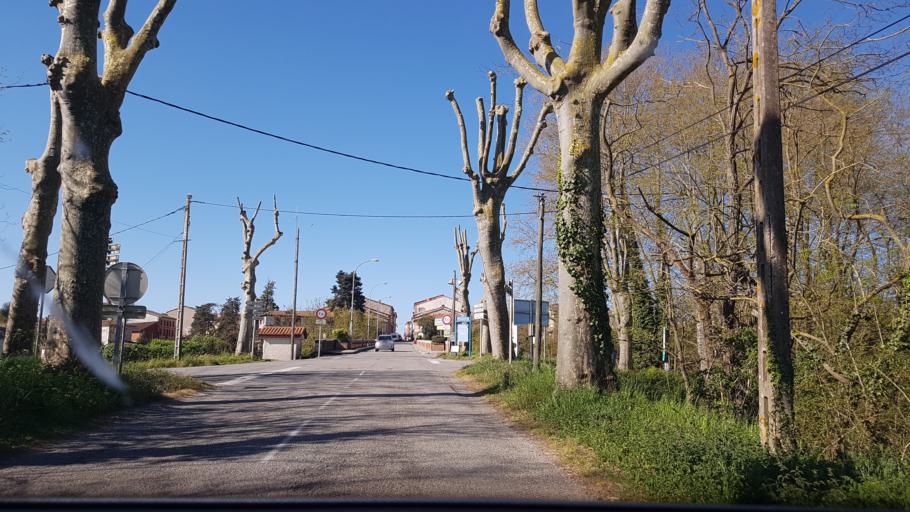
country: FR
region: Midi-Pyrenees
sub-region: Departement de l'Ariege
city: Mazeres
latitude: 43.2540
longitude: 1.6812
